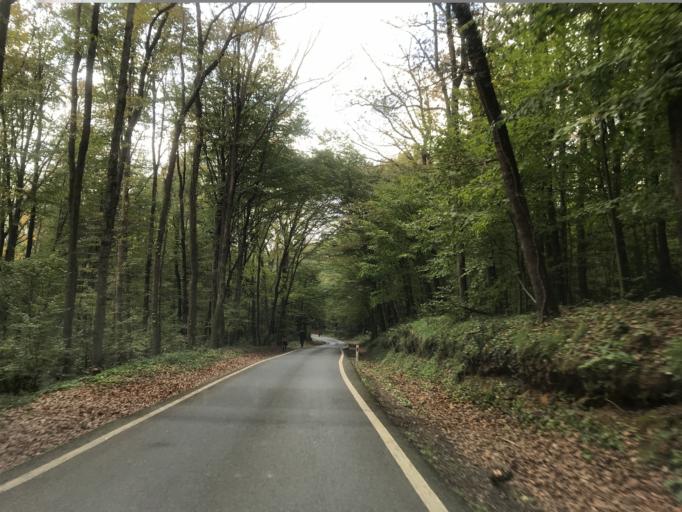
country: TR
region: Istanbul
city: Arikoey
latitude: 41.1893
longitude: 28.9795
